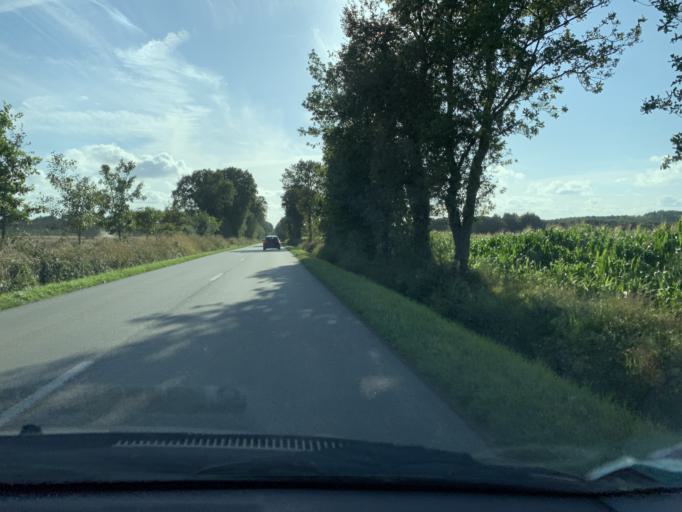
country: FR
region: Brittany
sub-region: Departement du Morbihan
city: Surzur
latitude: 47.5668
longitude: -2.6700
